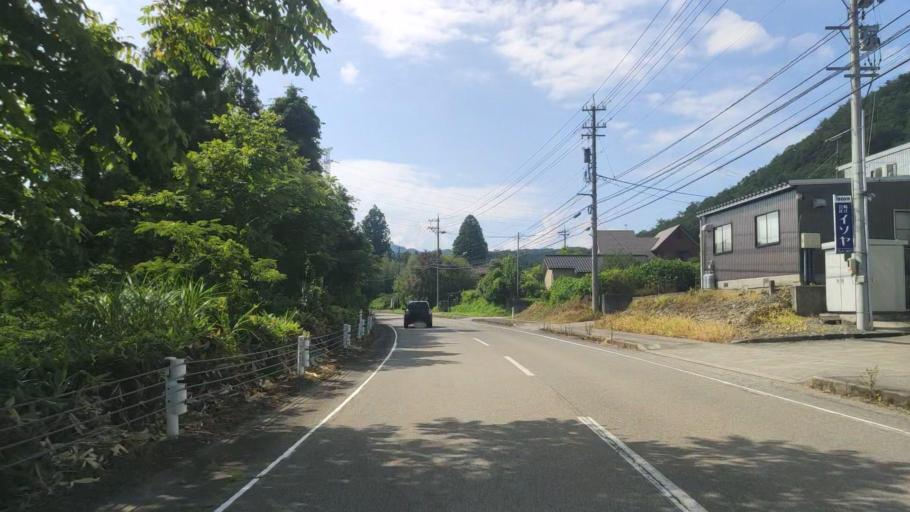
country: JP
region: Ishikawa
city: Komatsu
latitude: 36.3487
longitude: 136.5051
